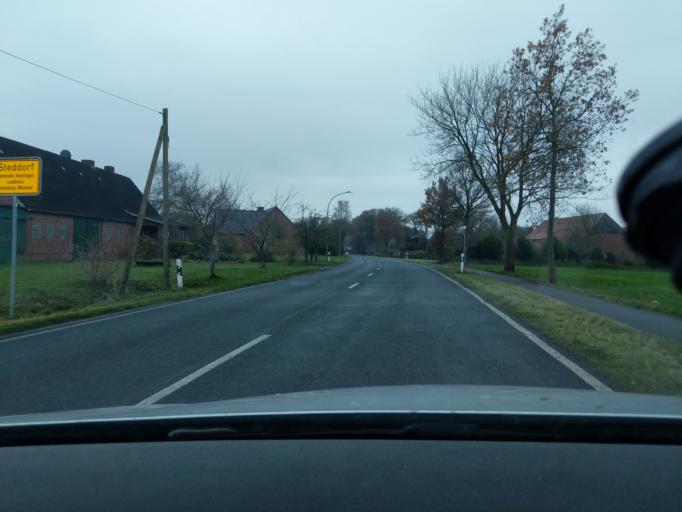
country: DE
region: Lower Saxony
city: Ahlerstedt
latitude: 53.3538
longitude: 9.4040
